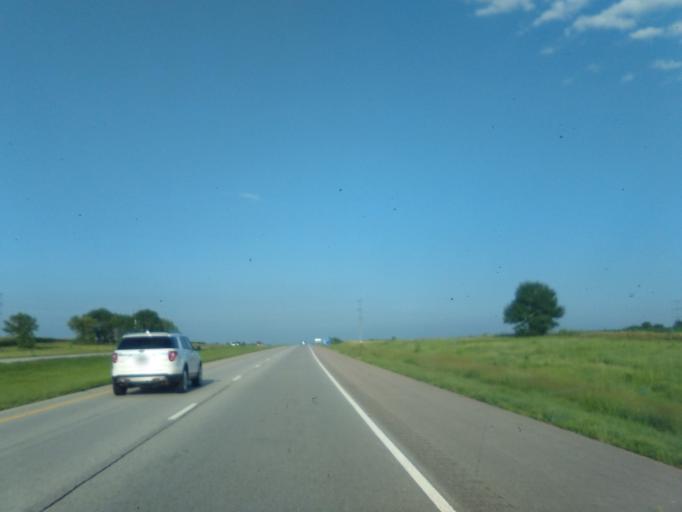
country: US
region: Nebraska
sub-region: Lancaster County
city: Lincoln
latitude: 40.8213
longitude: -96.8217
